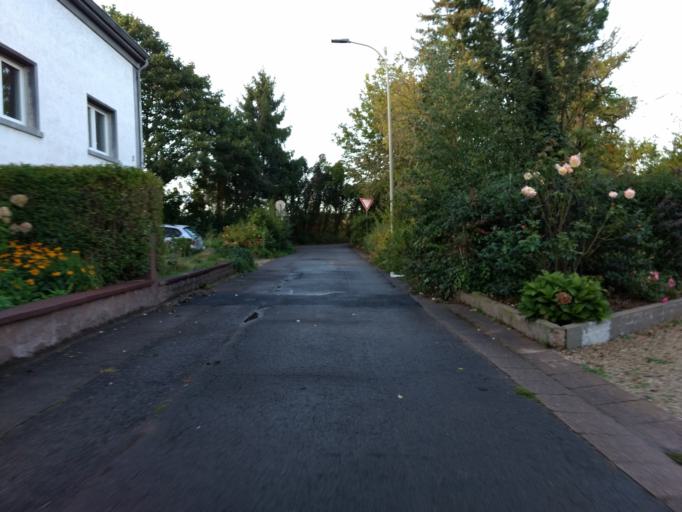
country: DE
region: Saarland
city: Nalbach
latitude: 49.3866
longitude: 6.7611
